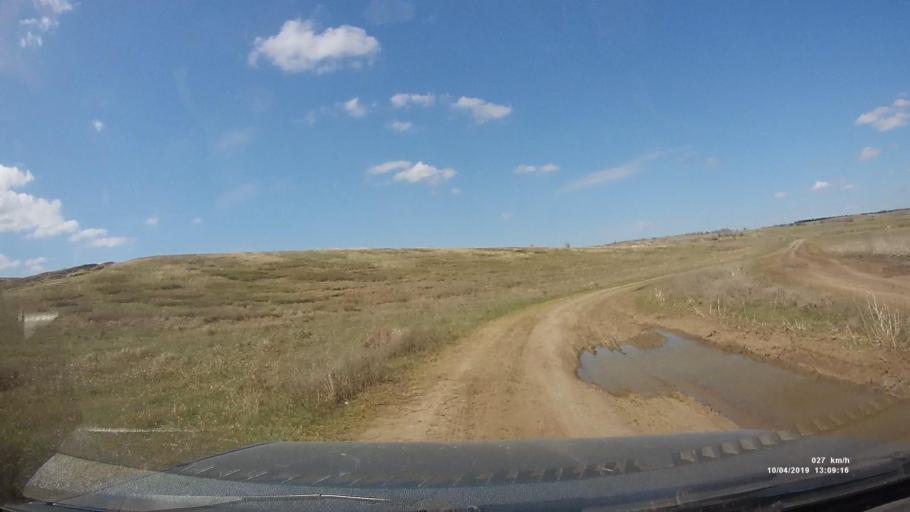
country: RU
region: Rostov
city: Masalovka
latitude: 48.4054
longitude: 40.2438
